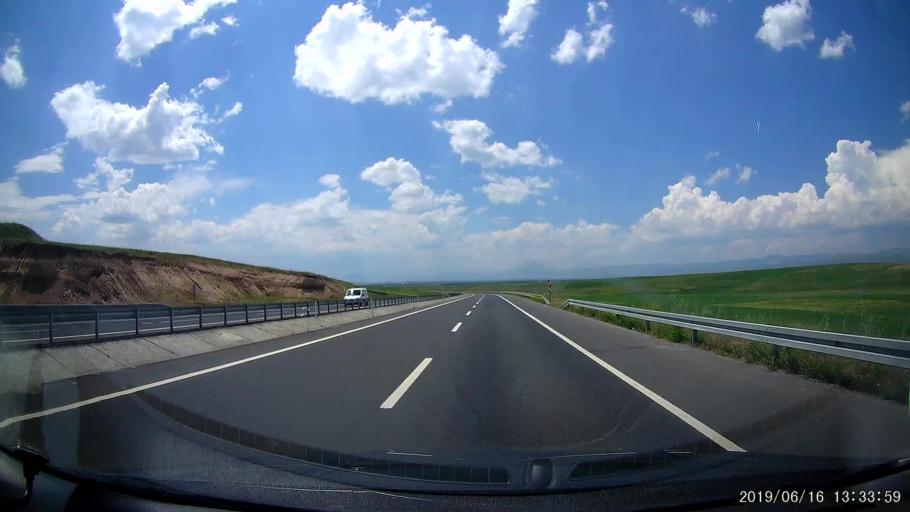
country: TR
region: Agri
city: Agri
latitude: 39.7103
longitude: 43.1393
